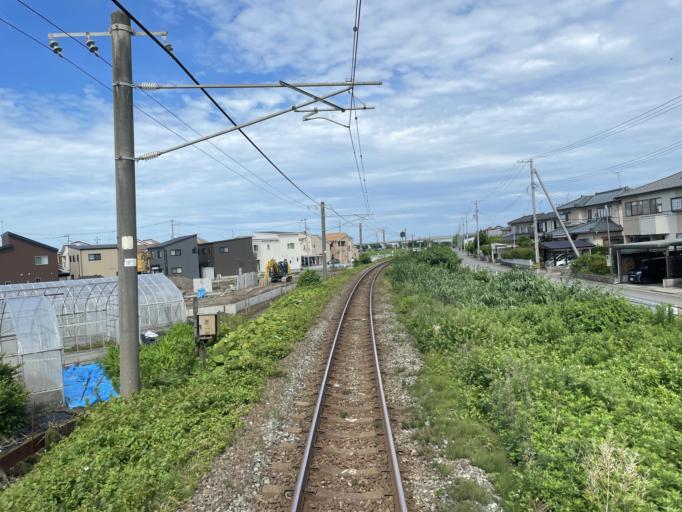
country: JP
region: Niigata
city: Suibara
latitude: 37.9156
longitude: 139.2077
